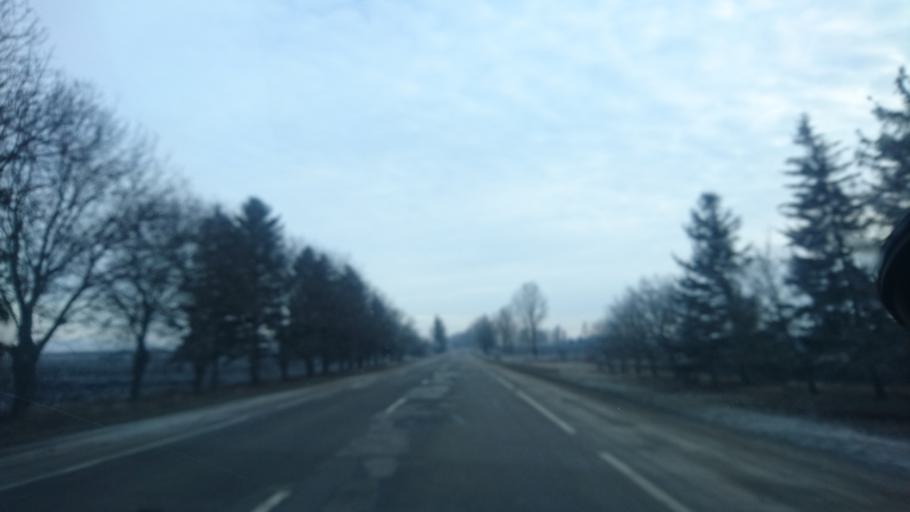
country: MD
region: Briceni
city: Briceni
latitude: 48.3317
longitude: 27.1204
